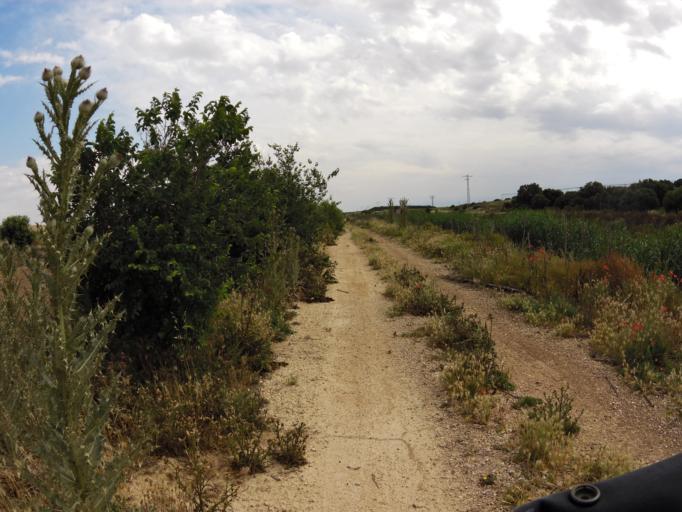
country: ES
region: Castille-La Mancha
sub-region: Provincia de Albacete
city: Albacete
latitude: 39.0468
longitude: -1.7619
